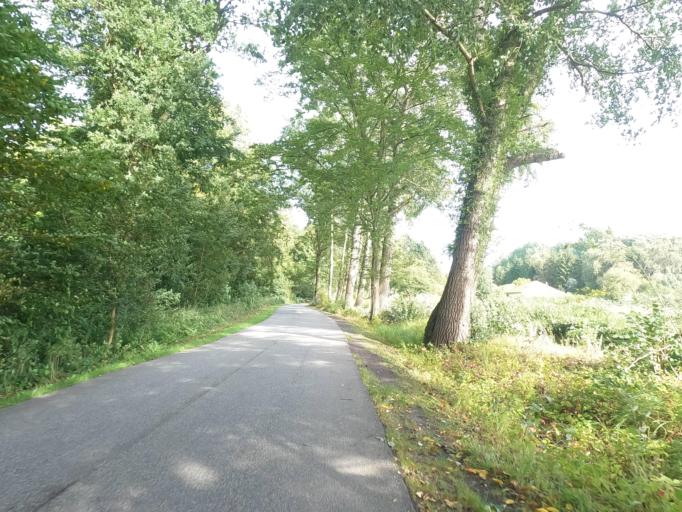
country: DE
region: Schleswig-Holstein
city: Gromitz
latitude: 54.1810
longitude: 10.9911
